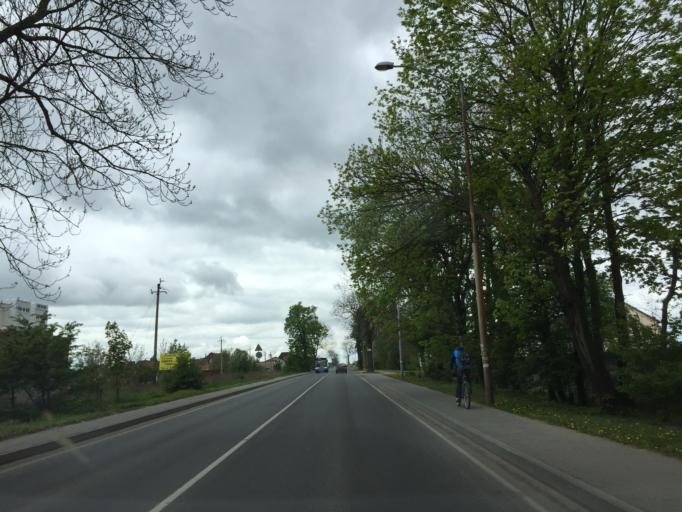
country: RU
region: Kaliningrad
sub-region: Gorod Kaliningrad
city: Kaliningrad
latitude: 54.6681
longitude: 20.4260
